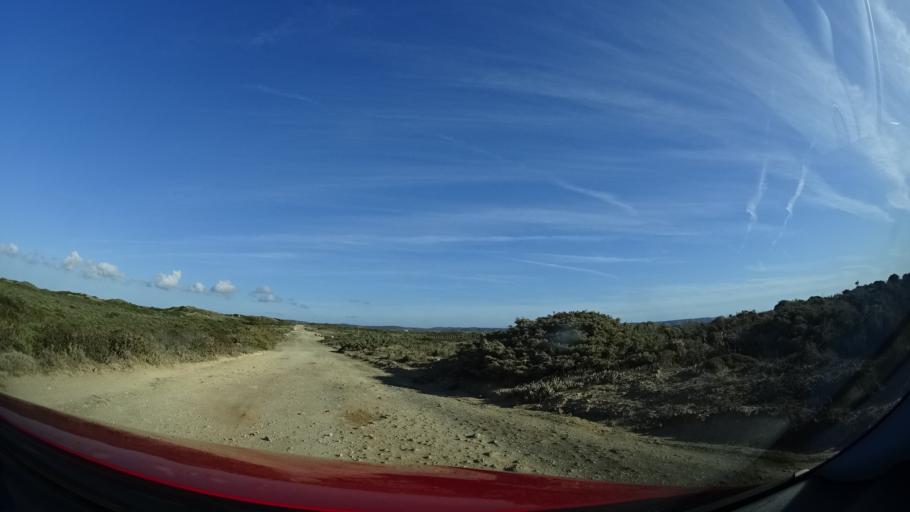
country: PT
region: Faro
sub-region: Vila do Bispo
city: Vila do Bispo
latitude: 37.1947
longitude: -8.9145
